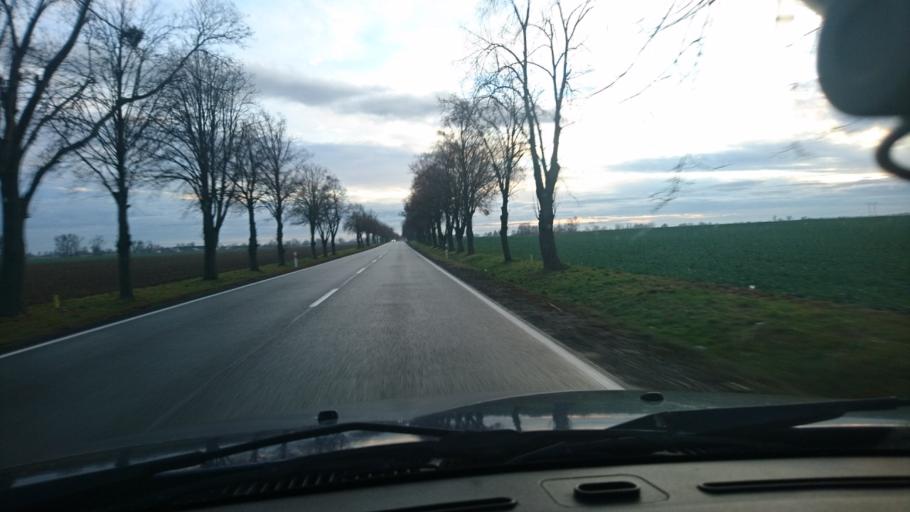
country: PL
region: Opole Voivodeship
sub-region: Powiat kluczborski
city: Kluczbork
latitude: 51.0406
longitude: 18.1947
